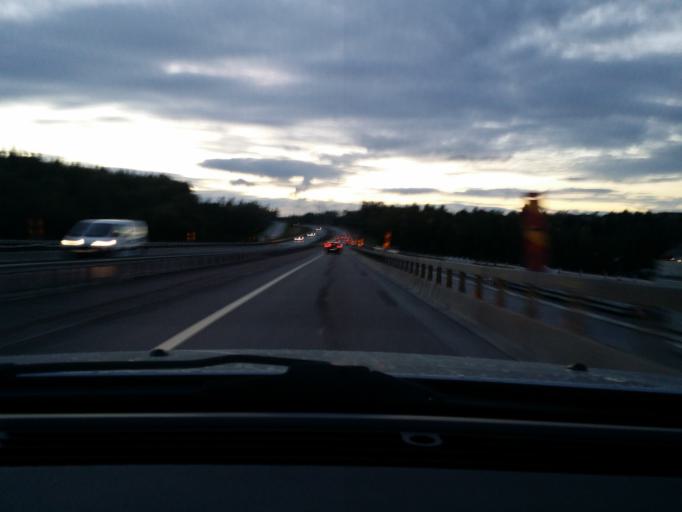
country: SE
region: Stockholm
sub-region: Upplands-Bro Kommun
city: Kungsaengen
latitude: 59.4793
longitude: 17.7878
